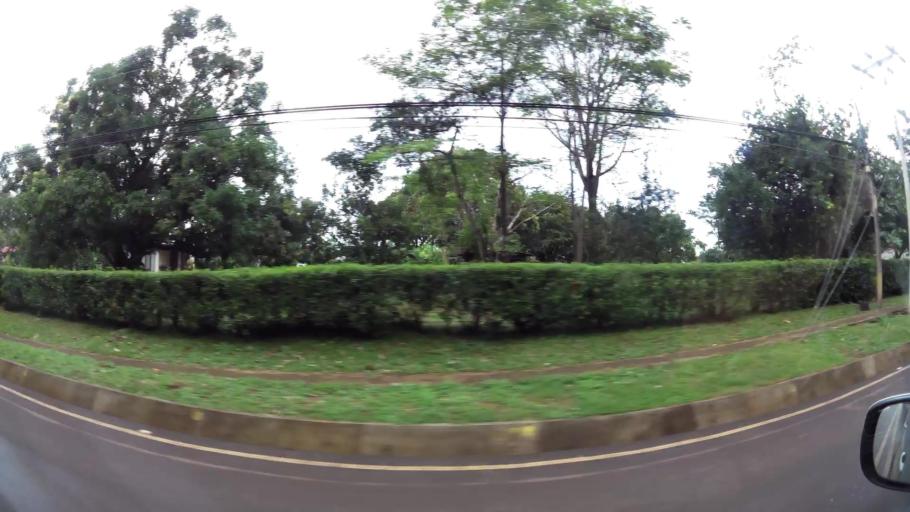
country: CR
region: Puntarenas
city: Esparza
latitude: 9.9599
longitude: -84.5934
